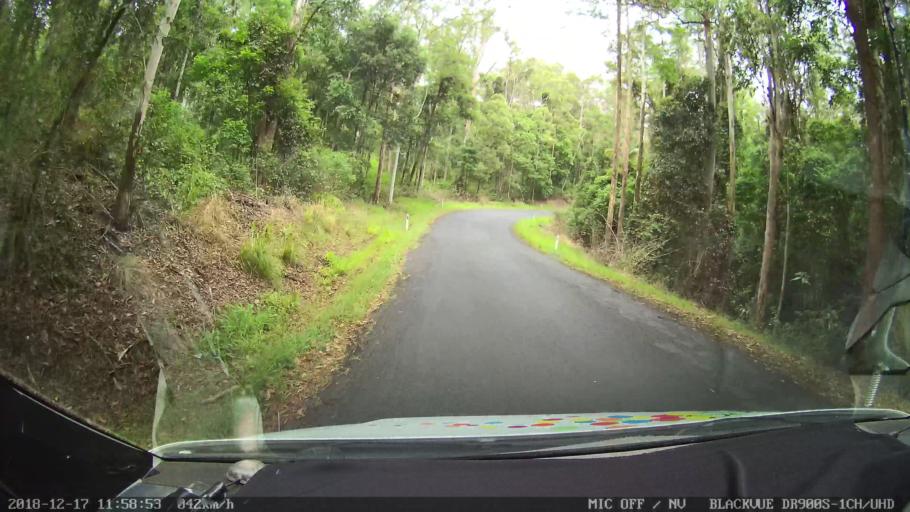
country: AU
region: New South Wales
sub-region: Kyogle
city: Kyogle
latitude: -28.5335
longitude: 152.5693
